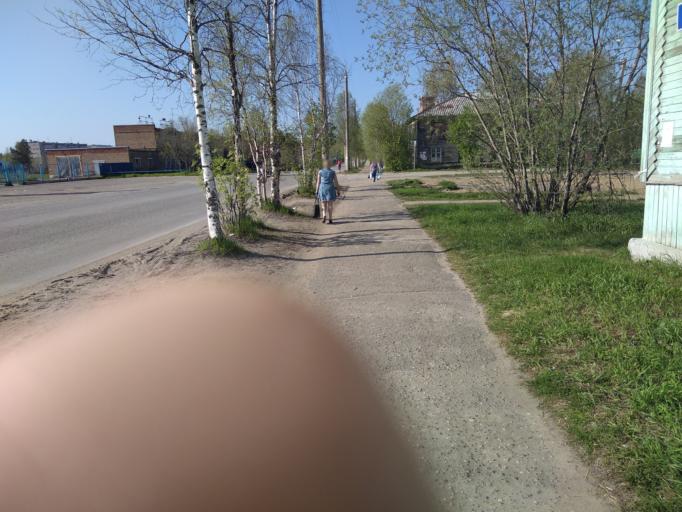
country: RU
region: Komi Republic
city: Pechora
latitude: 65.1193
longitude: 57.1543
